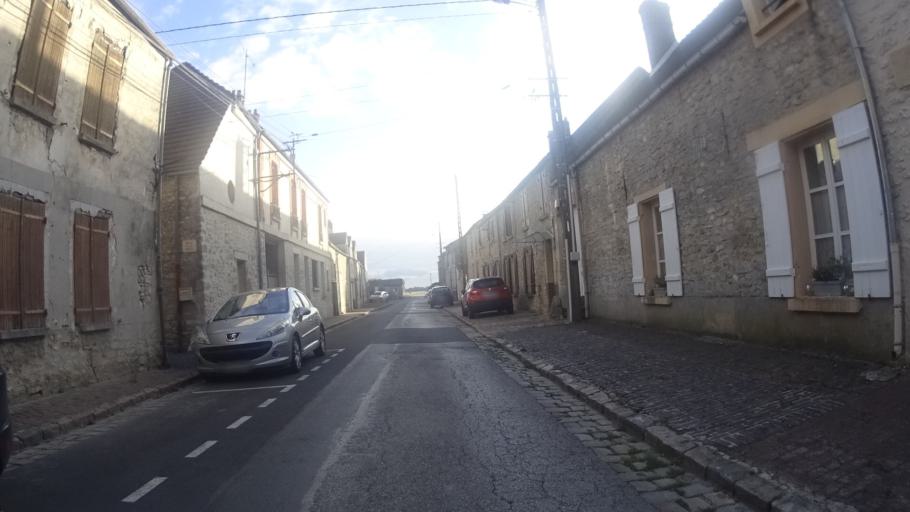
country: FR
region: Picardie
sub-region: Departement de l'Oise
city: Chamant
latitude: 49.2223
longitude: 2.6678
